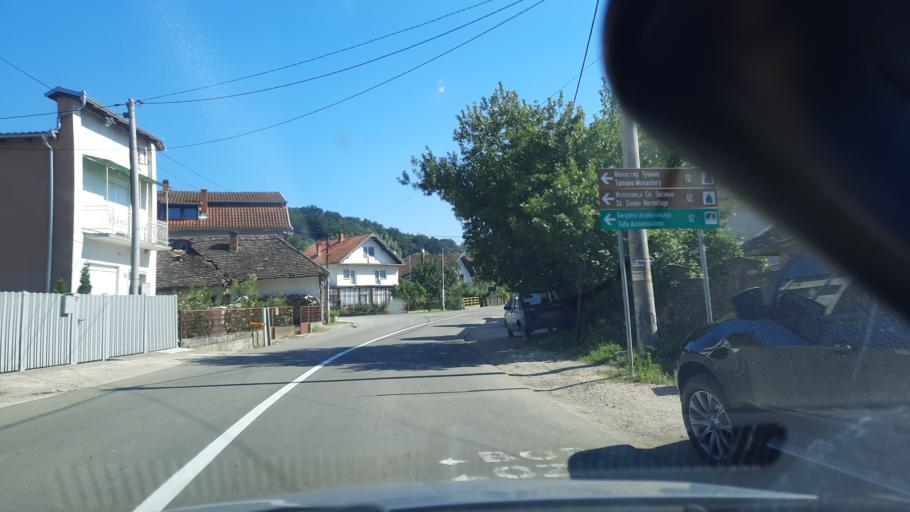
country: RS
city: Turija
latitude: 44.5217
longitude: 21.6403
